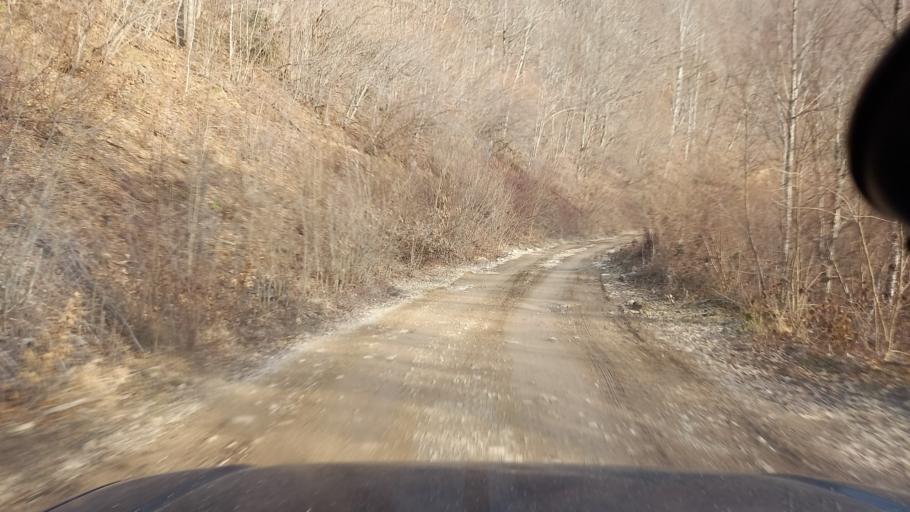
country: RU
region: Adygeya
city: Kamennomostskiy
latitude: 44.1498
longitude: 40.2998
